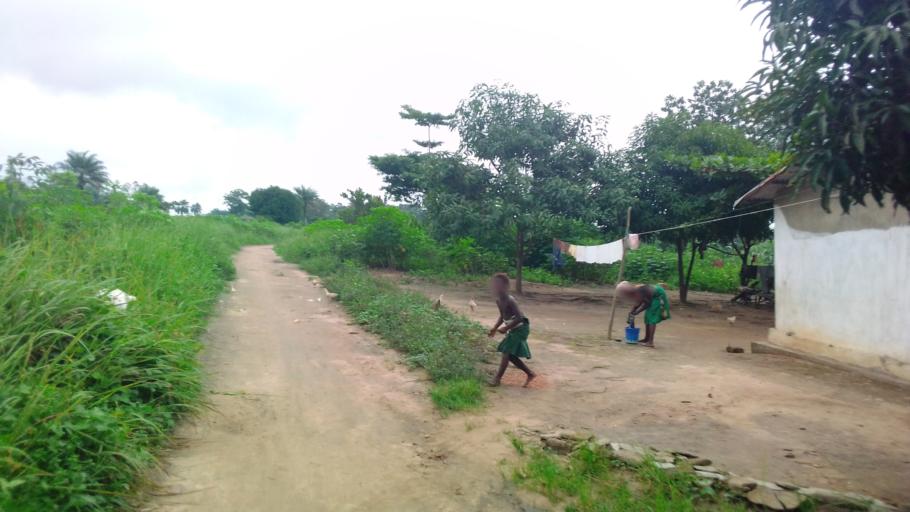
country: SL
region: Northern Province
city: Lunsar
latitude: 8.6944
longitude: -12.5482
